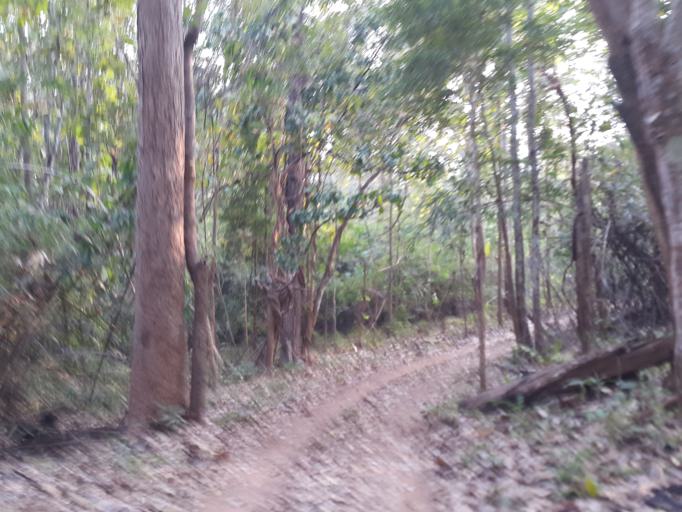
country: TH
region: Lamphun
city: Li
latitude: 17.6174
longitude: 98.9052
